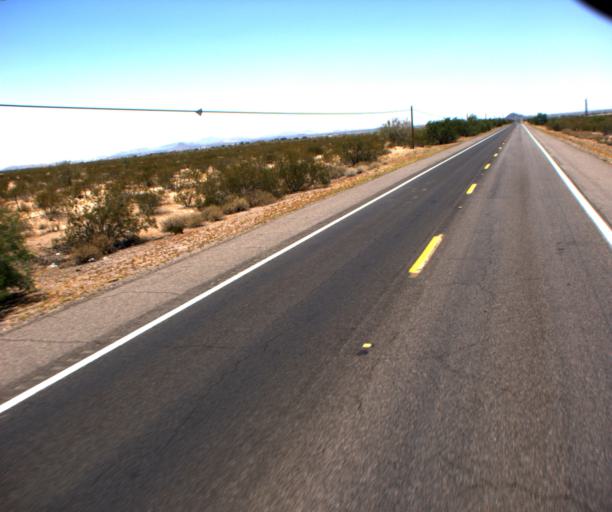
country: US
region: Arizona
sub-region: Pinal County
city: Florence
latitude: 32.9954
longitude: -111.3667
